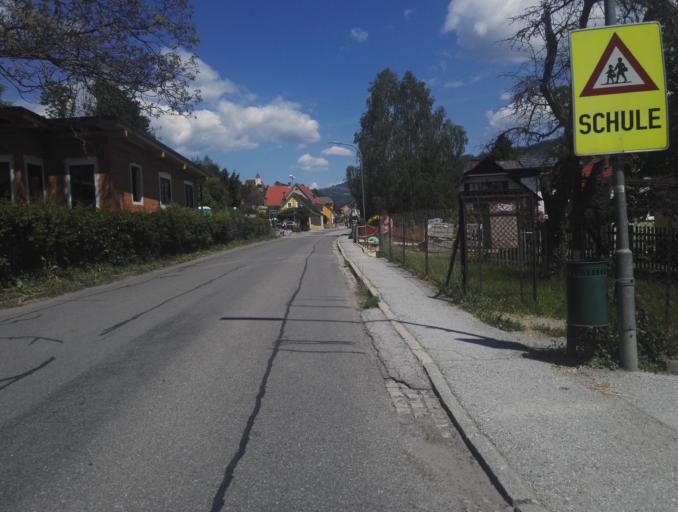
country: AT
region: Styria
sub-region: Politischer Bezirk Graz-Umgebung
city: Deutschfeistritz
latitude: 47.1947
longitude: 15.3357
